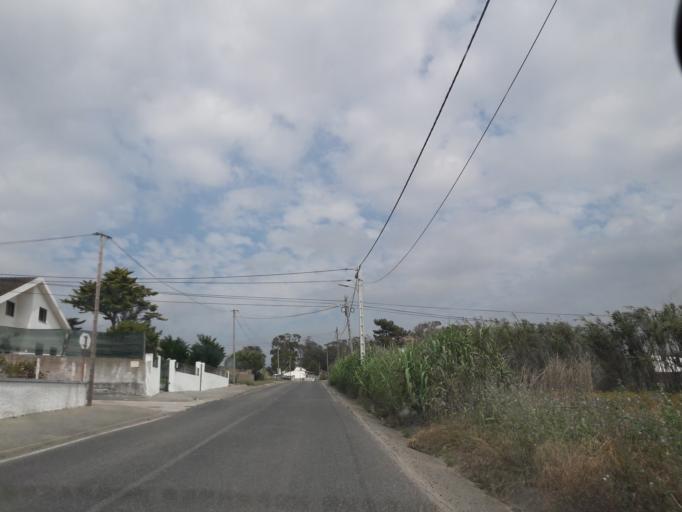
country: PT
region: Leiria
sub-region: Peniche
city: Atouguia da Baleia
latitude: 39.3610
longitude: -9.3101
